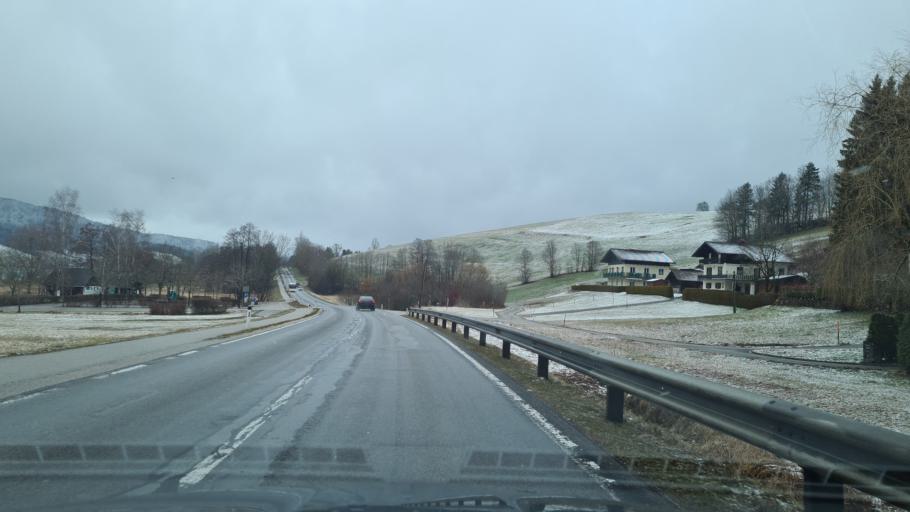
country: AT
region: Upper Austria
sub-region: Politischer Bezirk Vocklabruck
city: Zell am Moos
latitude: 47.8902
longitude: 13.3184
